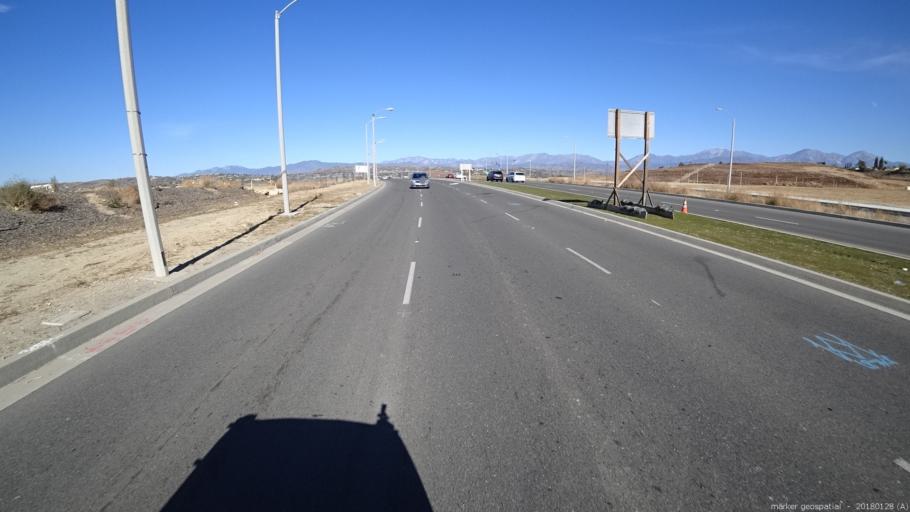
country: US
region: California
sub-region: Los Angeles County
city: Diamond Bar
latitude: 34.0158
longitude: -117.8247
